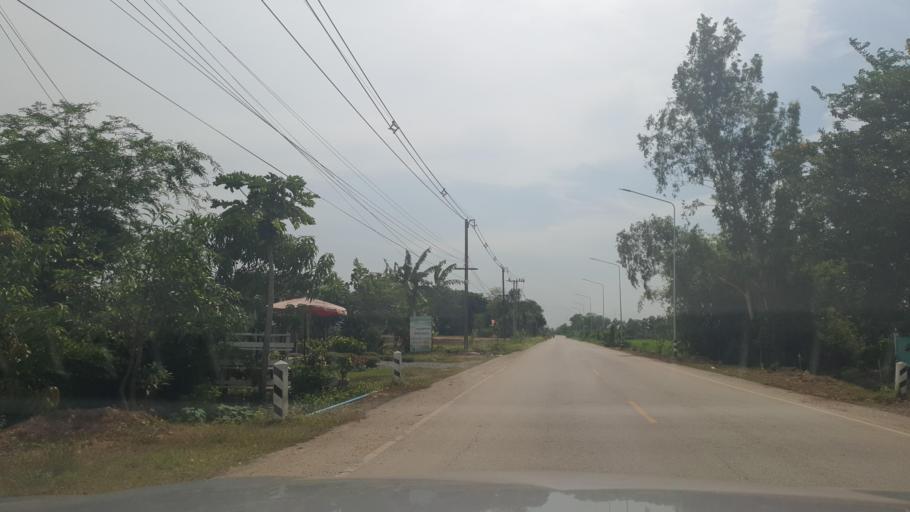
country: TH
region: Sukhothai
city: Si Samrong
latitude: 17.1394
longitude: 99.8449
